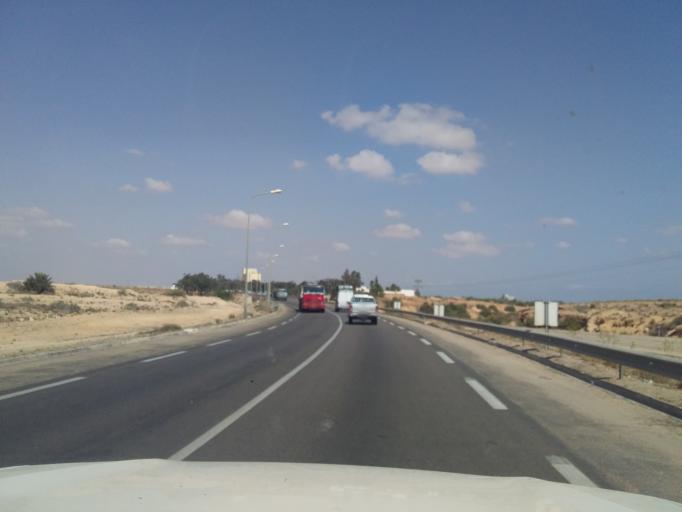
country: TN
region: Madanin
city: Medenine
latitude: 33.5929
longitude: 10.3135
